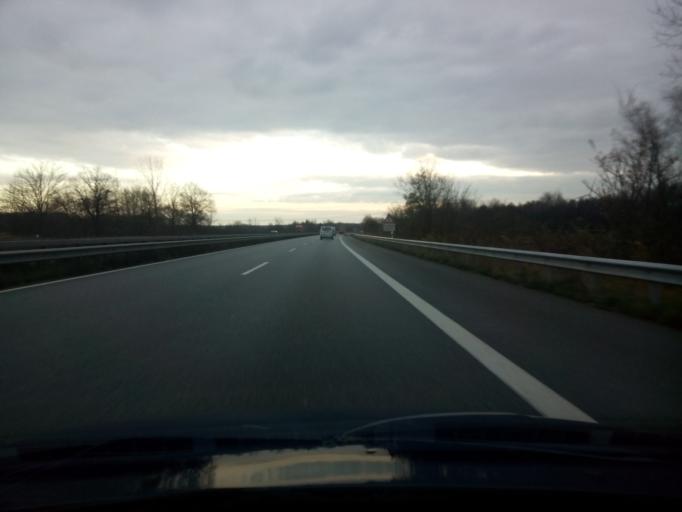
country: DE
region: Lower Saxony
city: Uthlede
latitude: 53.3292
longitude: 8.6174
